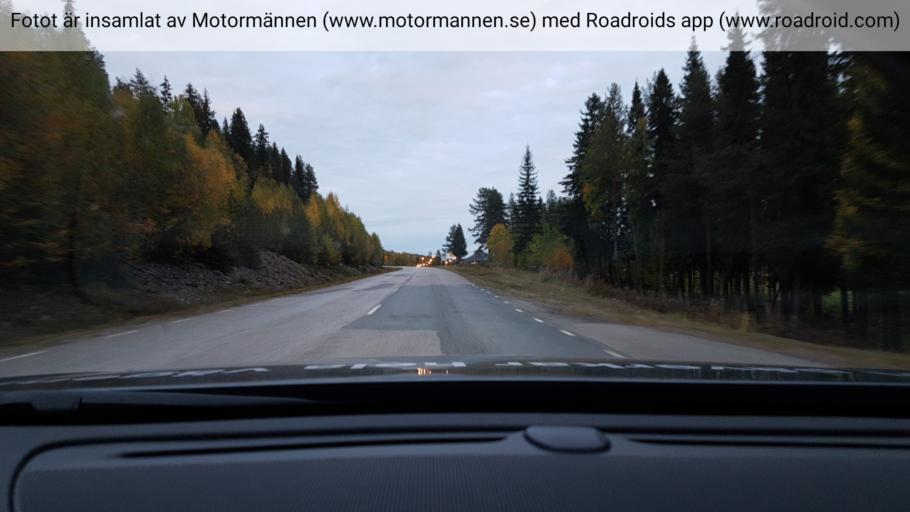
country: SE
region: Norrbotten
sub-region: Alvsbyns Kommun
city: AElvsbyn
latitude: 65.8602
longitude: 20.4166
